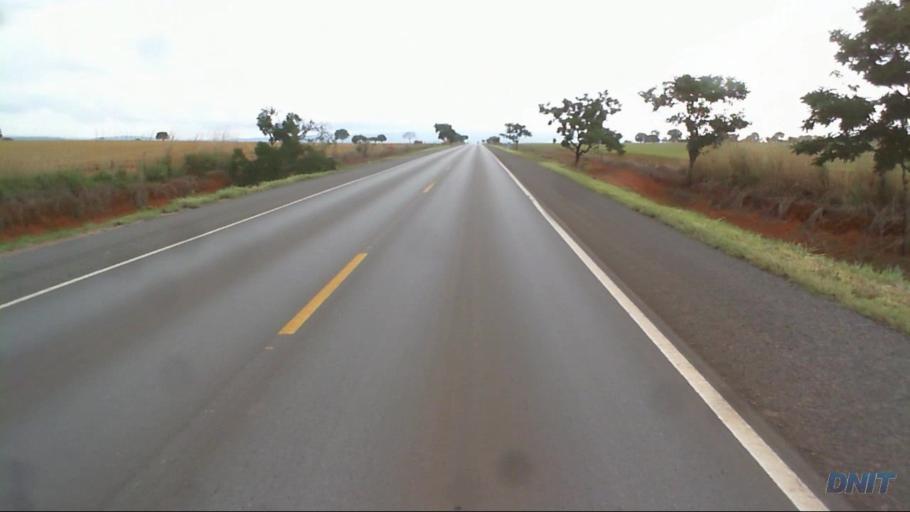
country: BR
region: Goias
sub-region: Padre Bernardo
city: Padre Bernardo
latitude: -15.2179
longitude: -48.6174
